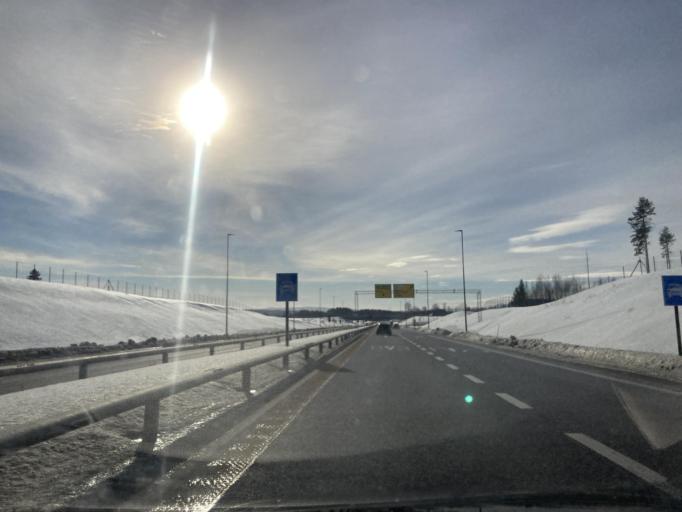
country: NO
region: Hedmark
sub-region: Loten
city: Loten
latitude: 60.8311
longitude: 11.2931
